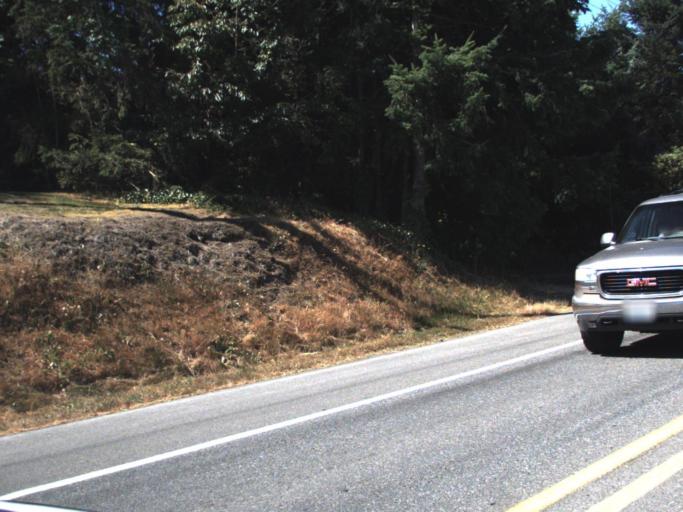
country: US
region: Washington
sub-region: King County
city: Enumclaw
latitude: 47.1992
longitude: -121.9671
